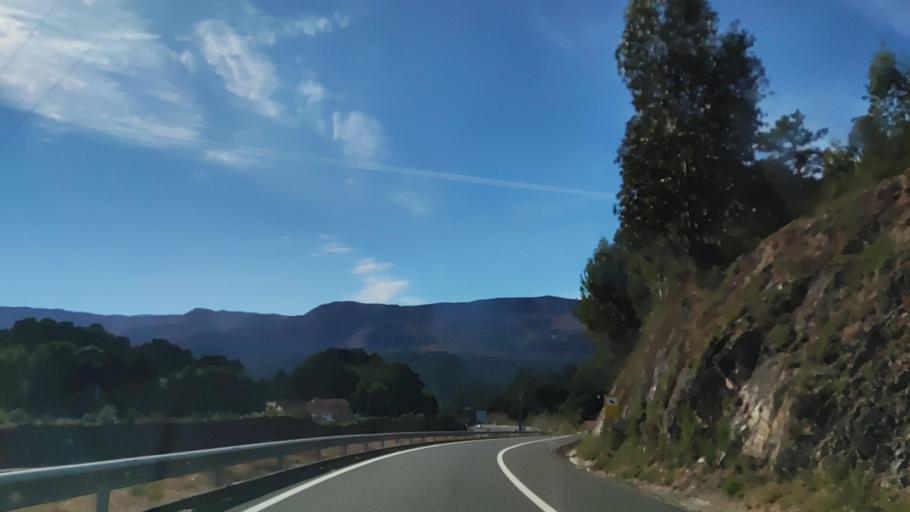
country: ES
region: Galicia
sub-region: Provincia da Coruna
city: Boiro
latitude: 42.6578
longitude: -8.8814
